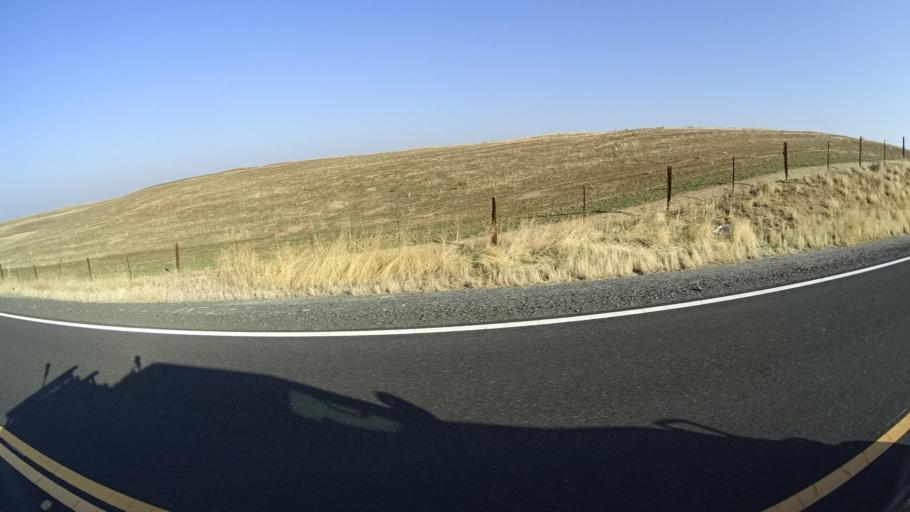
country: US
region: California
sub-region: Tulare County
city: Richgrove
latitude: 35.7510
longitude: -118.9992
